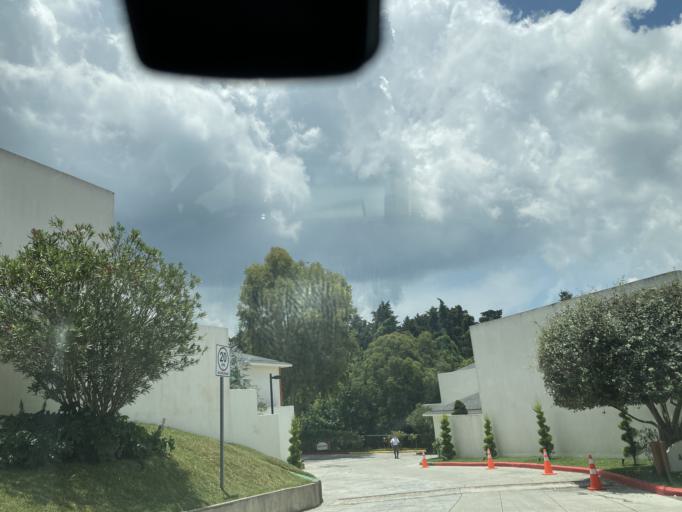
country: GT
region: Guatemala
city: Fraijanes
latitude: 14.5067
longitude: -90.4600
